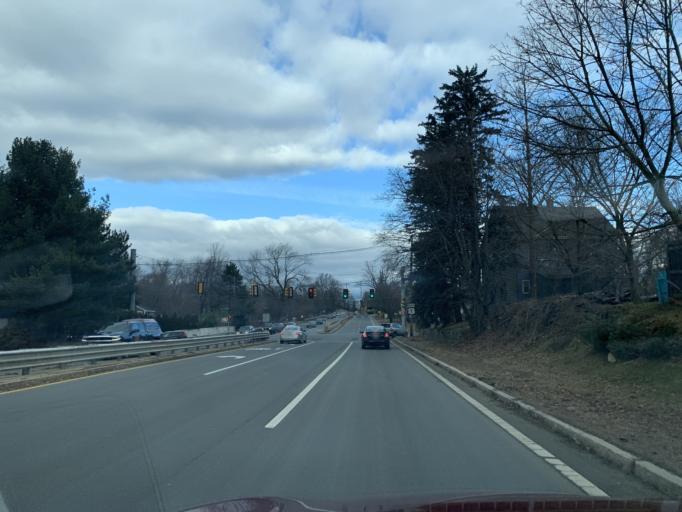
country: US
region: Massachusetts
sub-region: Essex County
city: Newburyport
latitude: 42.8061
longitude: -70.8784
